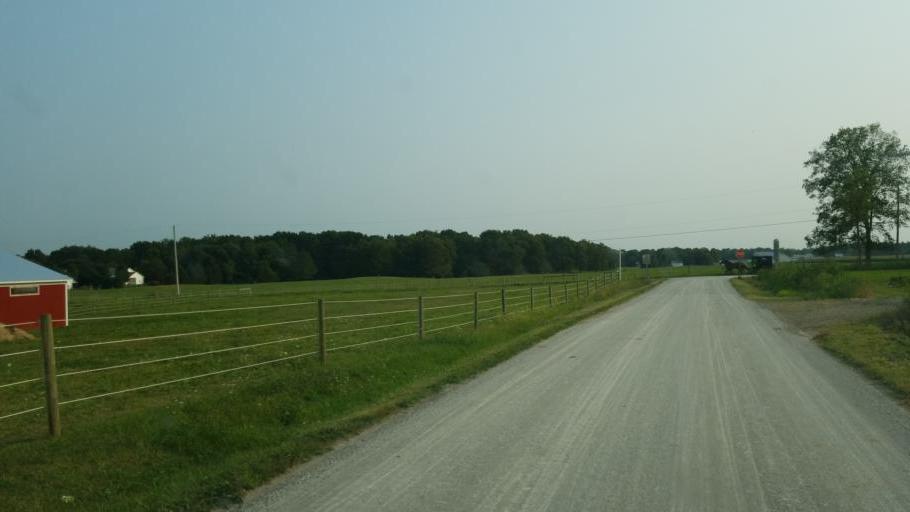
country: US
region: Ohio
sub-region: Geauga County
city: Middlefield
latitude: 41.4682
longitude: -80.9701
